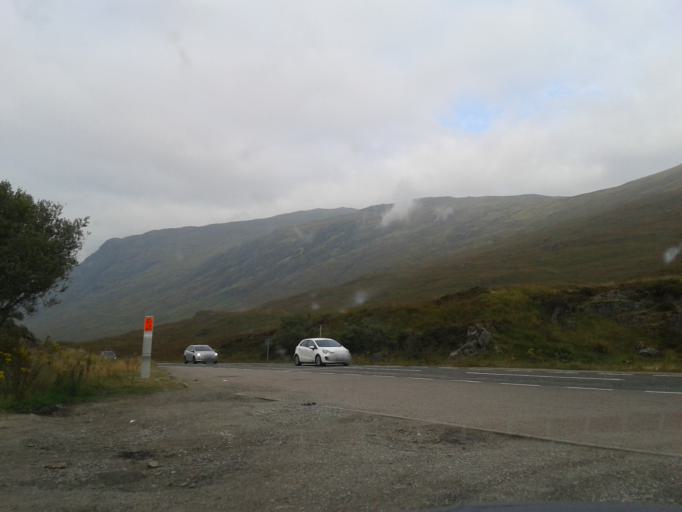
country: GB
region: Scotland
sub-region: Highland
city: Spean Bridge
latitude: 56.6614
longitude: -4.9174
